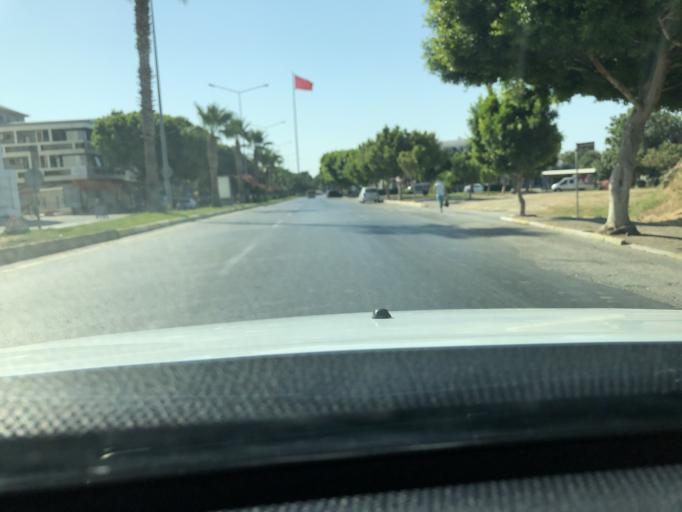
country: TR
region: Antalya
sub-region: Manavgat
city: Side
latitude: 36.7787
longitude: 31.3955
